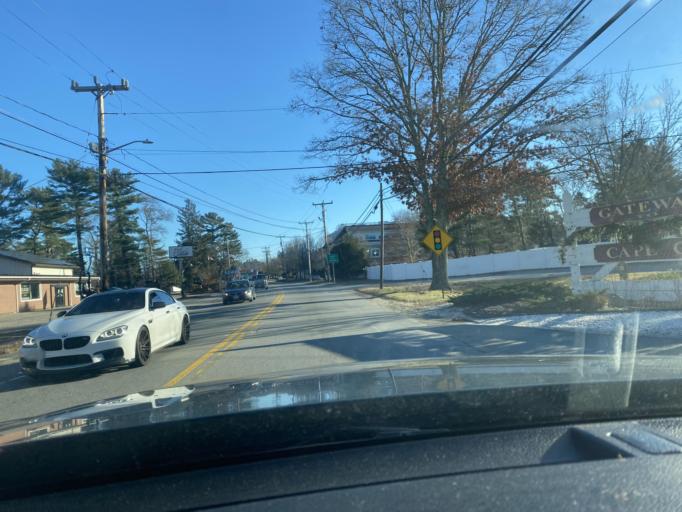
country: US
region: Massachusetts
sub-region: Plymouth County
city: Wareham Center
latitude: 41.7704
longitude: -70.7337
